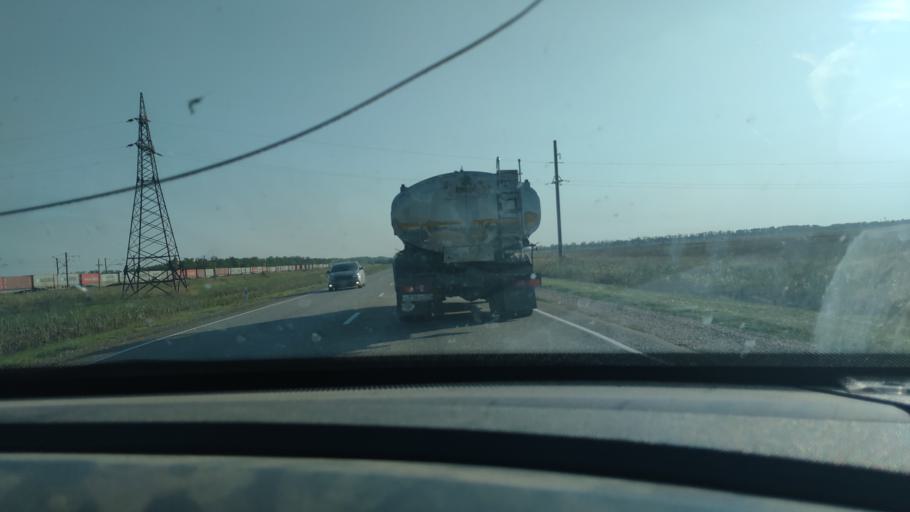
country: RU
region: Krasnodarskiy
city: Starominskaya
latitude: 46.4402
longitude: 39.0221
